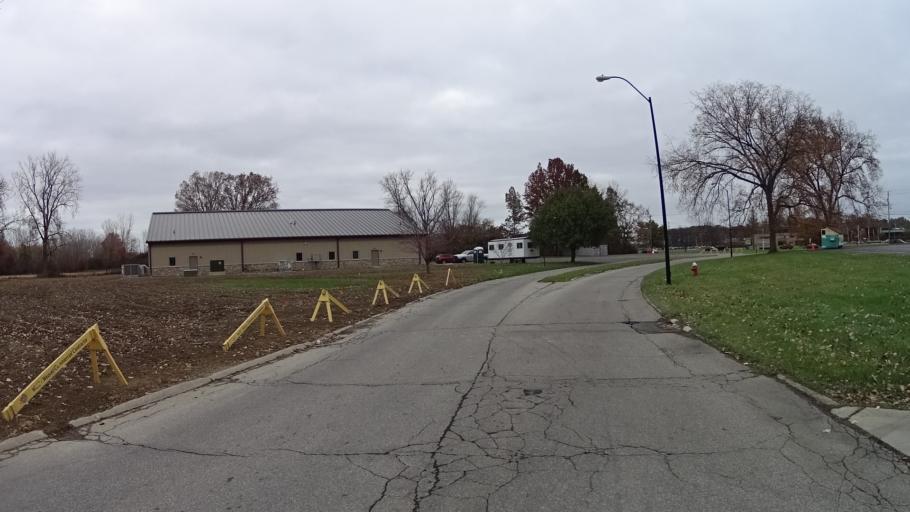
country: US
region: Ohio
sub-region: Lorain County
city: Sheffield
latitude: 41.4123
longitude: -82.0787
